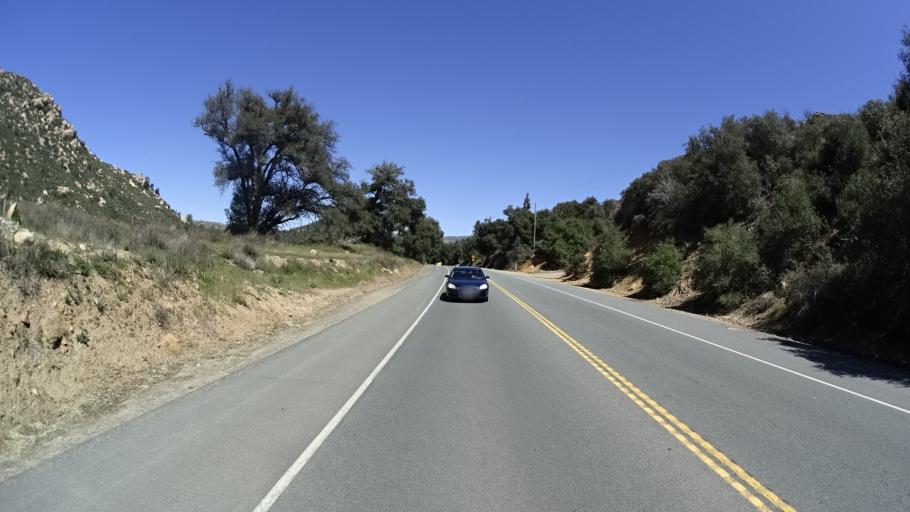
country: US
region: California
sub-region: San Diego County
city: Descanso
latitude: 32.8383
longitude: -116.6161
